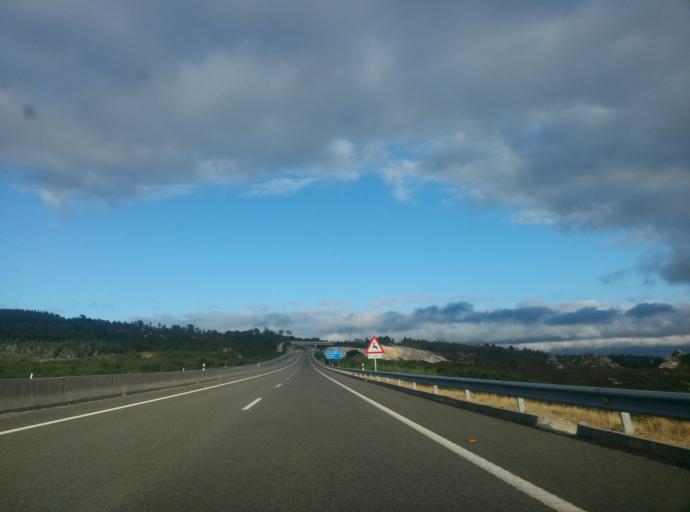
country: ES
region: Galicia
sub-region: Provincia de Lugo
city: Vilalba
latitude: 43.3600
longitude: -7.7626
